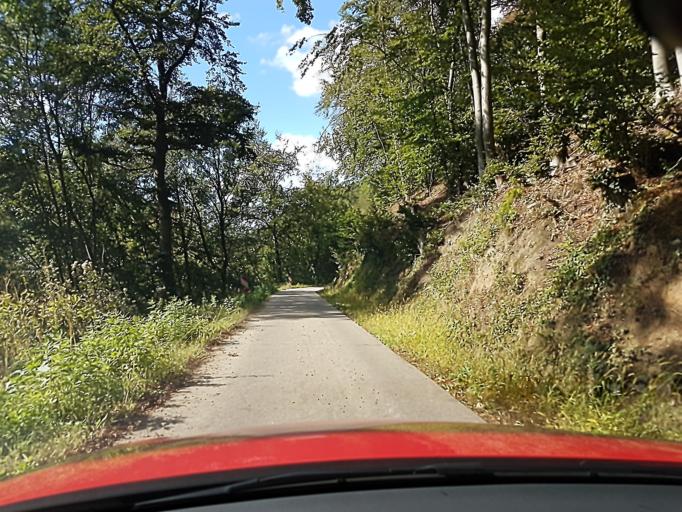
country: DE
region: Hesse
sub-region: Regierungsbezirk Darmstadt
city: Bensheim
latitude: 49.7059
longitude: 8.6408
